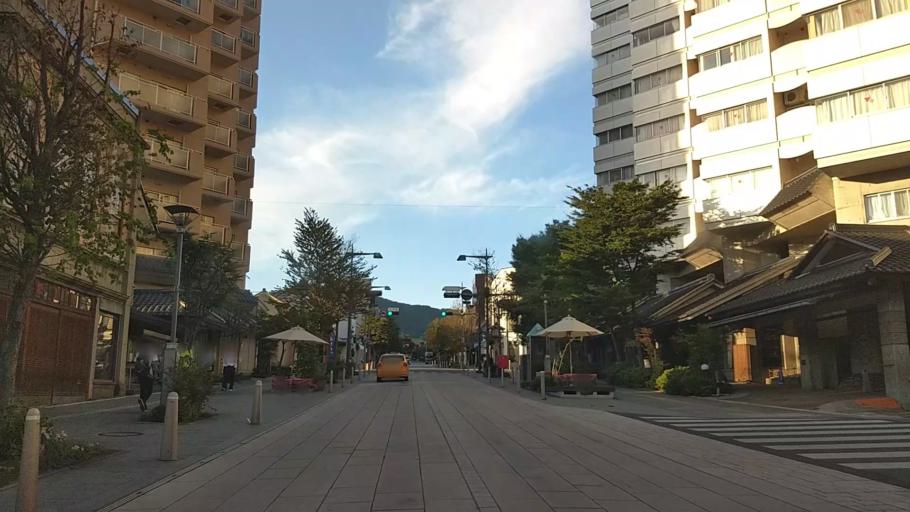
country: JP
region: Nagano
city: Nagano-shi
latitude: 36.6539
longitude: 138.1873
